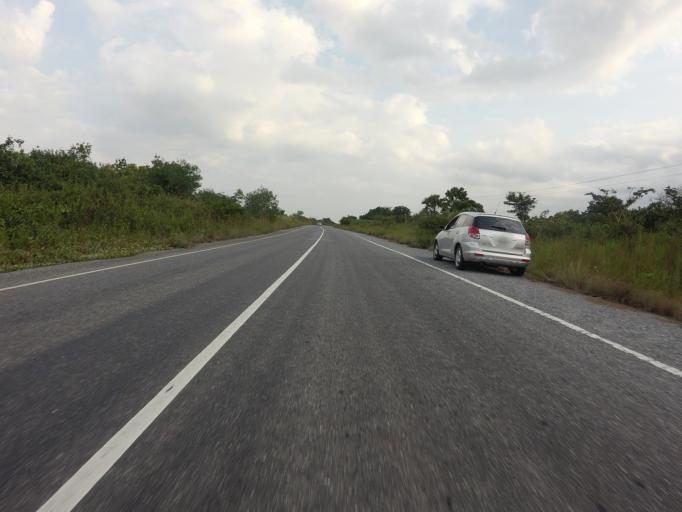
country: GH
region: Volta
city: Ho
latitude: 6.3539
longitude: 0.5371
